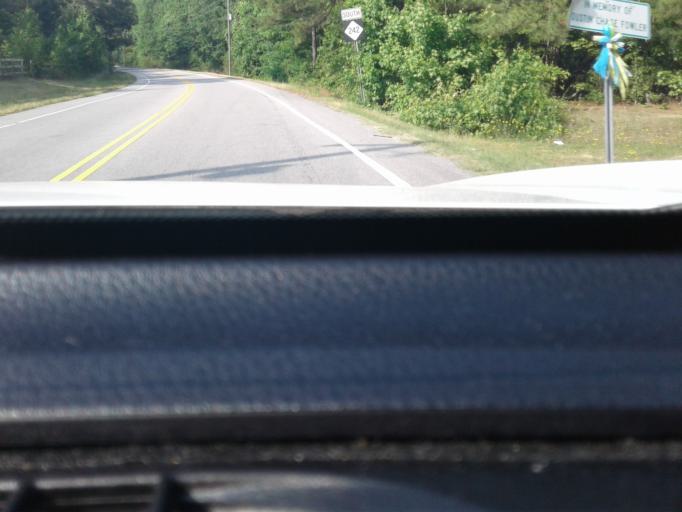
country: US
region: North Carolina
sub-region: Johnston County
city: Benson
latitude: 35.4169
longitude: -78.5393
